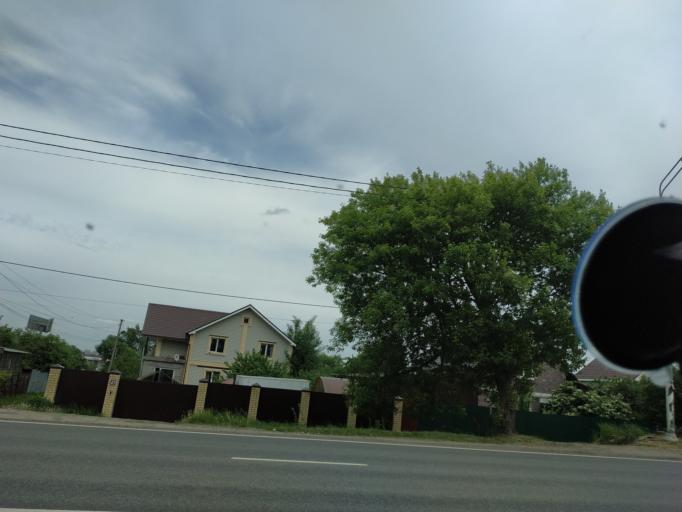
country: RU
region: Moskovskaya
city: Ostrovtsy
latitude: 55.5604
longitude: 38.0500
